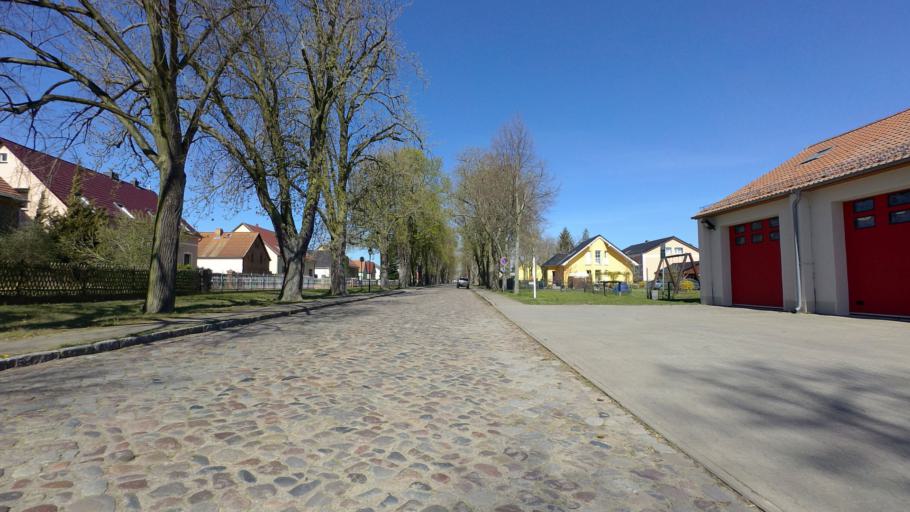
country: DE
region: Brandenburg
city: Rangsdorf
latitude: 52.3225
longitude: 13.4657
